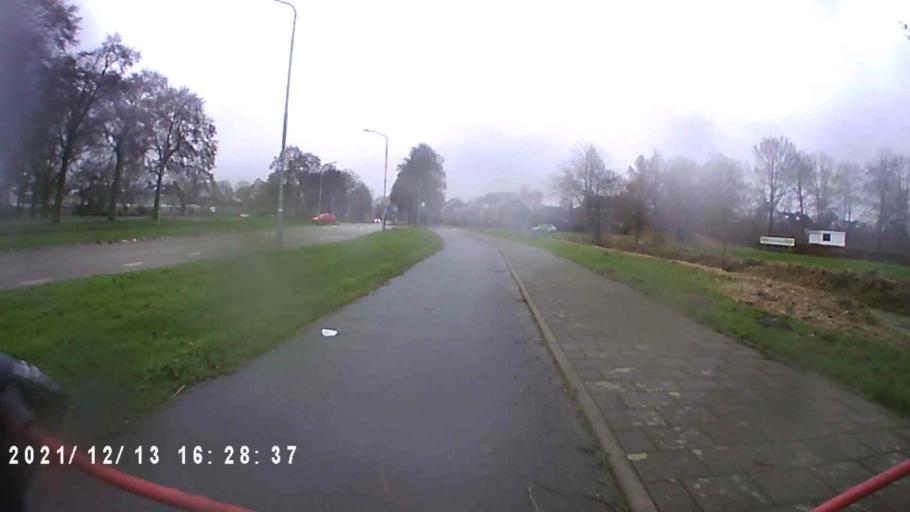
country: NL
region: Groningen
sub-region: Gemeente Appingedam
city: Appingedam
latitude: 53.3258
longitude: 6.8876
